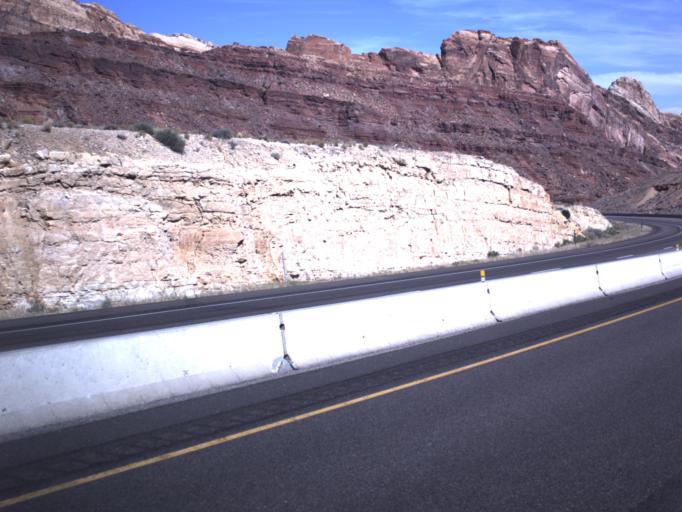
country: US
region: Utah
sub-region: Carbon County
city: East Carbon City
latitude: 38.9289
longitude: -110.4635
